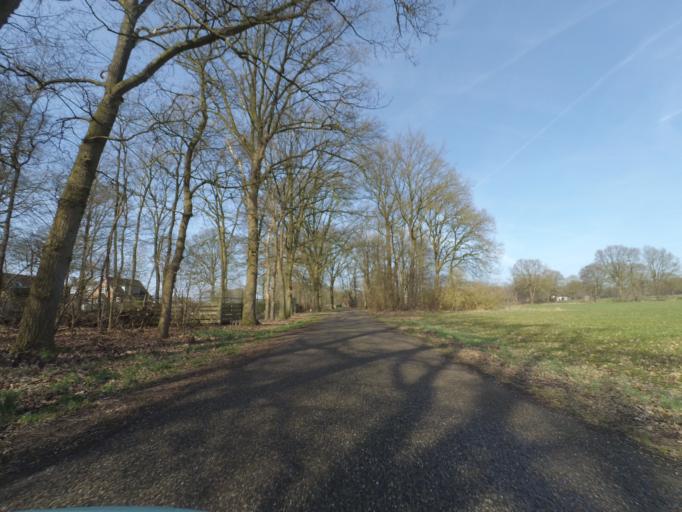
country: NL
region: Gelderland
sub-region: Gemeente Barneveld
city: Voorthuizen
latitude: 52.2096
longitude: 5.6330
